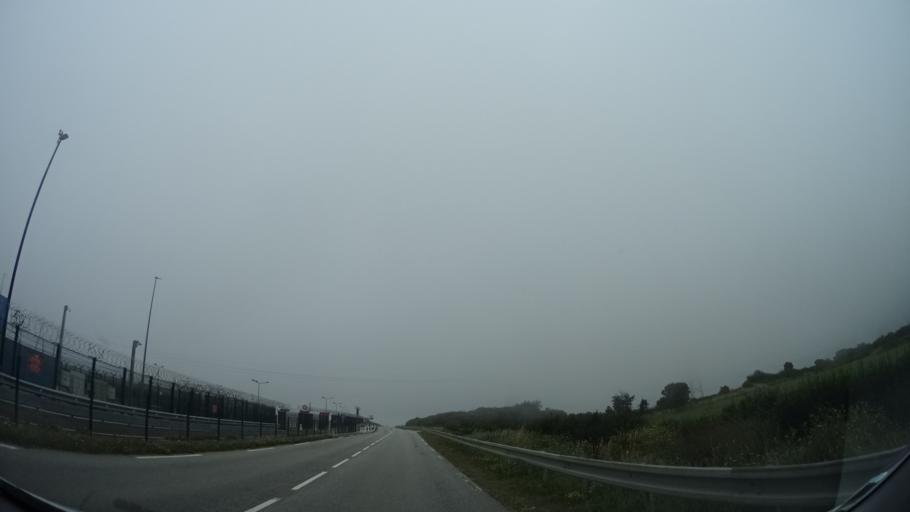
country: FR
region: Lower Normandy
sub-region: Departement de la Manche
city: Flamanville
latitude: 49.5345
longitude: -1.8781
